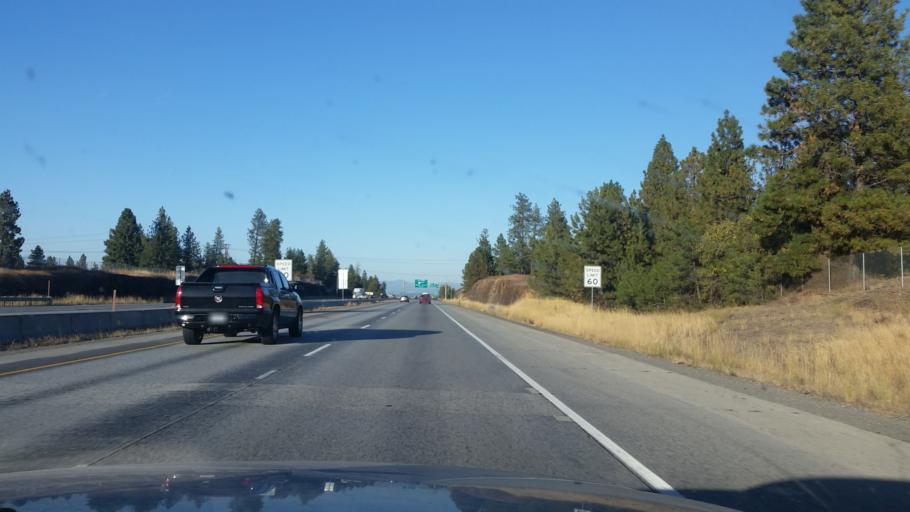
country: US
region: Washington
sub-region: Spokane County
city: Spokane
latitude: 47.6268
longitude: -117.4910
